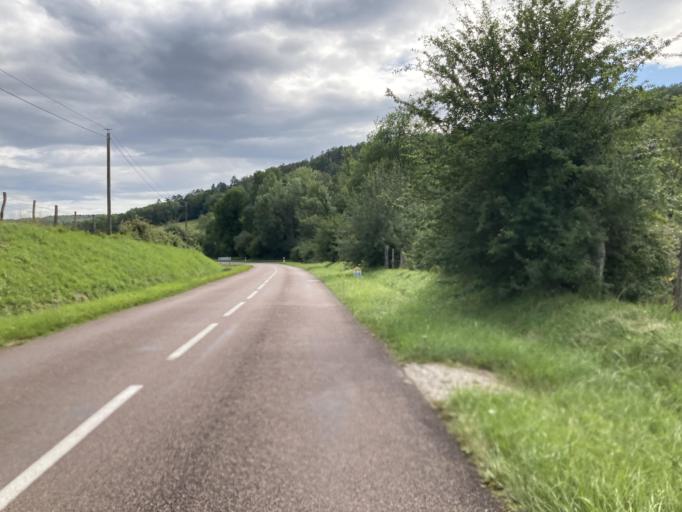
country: FR
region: Bourgogne
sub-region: Departement de la Cote-d'Or
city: Montbard
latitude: 47.6298
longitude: 4.3678
